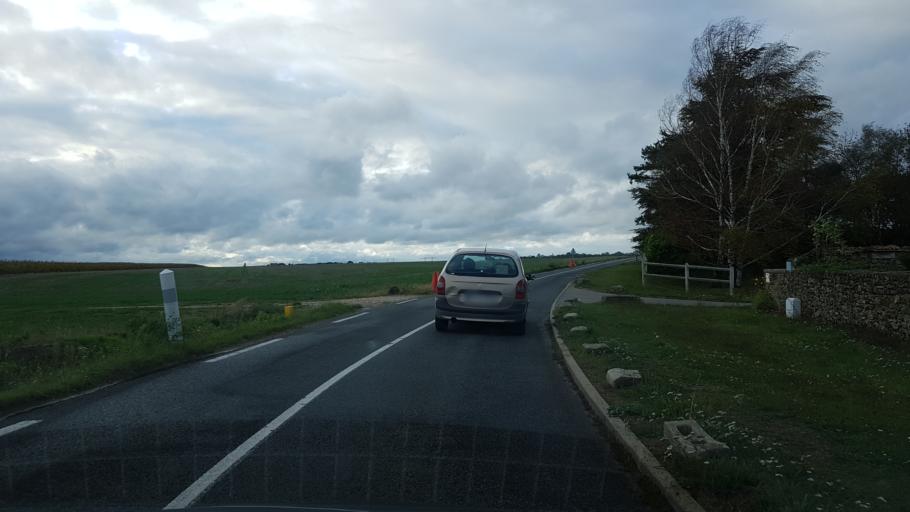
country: FR
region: Ile-de-France
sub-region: Departement de l'Essonne
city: Gometz-la-Ville
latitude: 48.6601
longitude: 2.1376
